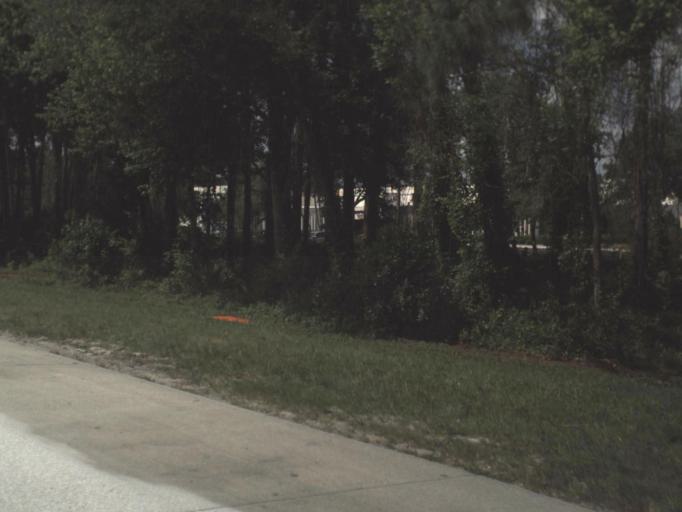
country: US
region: Florida
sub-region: Saint Johns County
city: Fruit Cove
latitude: 30.2068
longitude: -81.5619
